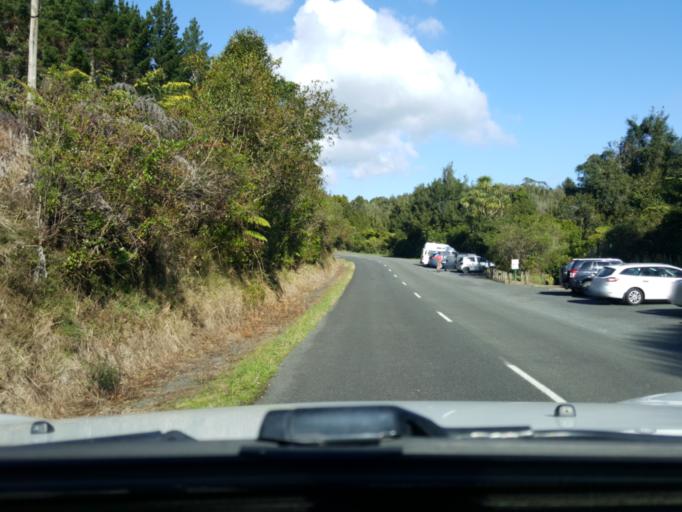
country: NZ
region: Waikato
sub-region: Waikato District
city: Raglan
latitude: -37.9069
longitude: 174.9012
